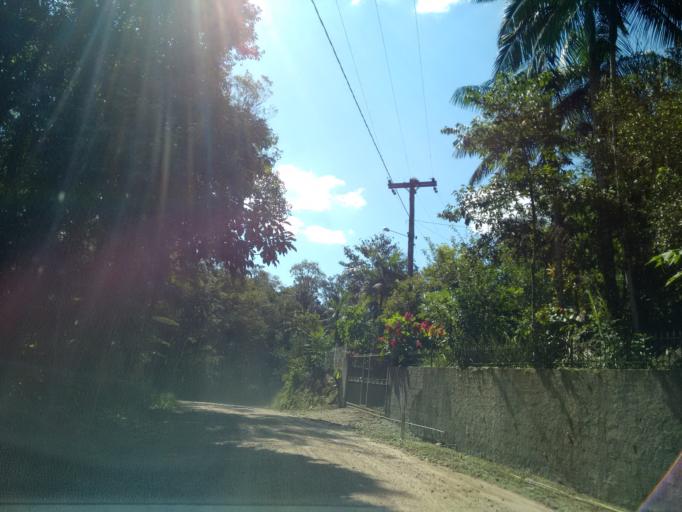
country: BR
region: Santa Catarina
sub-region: Indaial
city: Indaial
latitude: -26.9429
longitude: -49.1807
